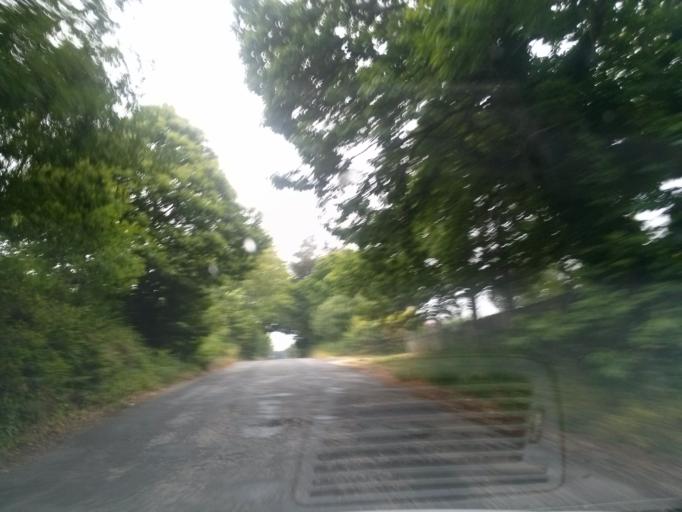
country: ES
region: Galicia
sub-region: Provincia de Lugo
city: Rabade
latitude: 43.1126
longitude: -7.6151
